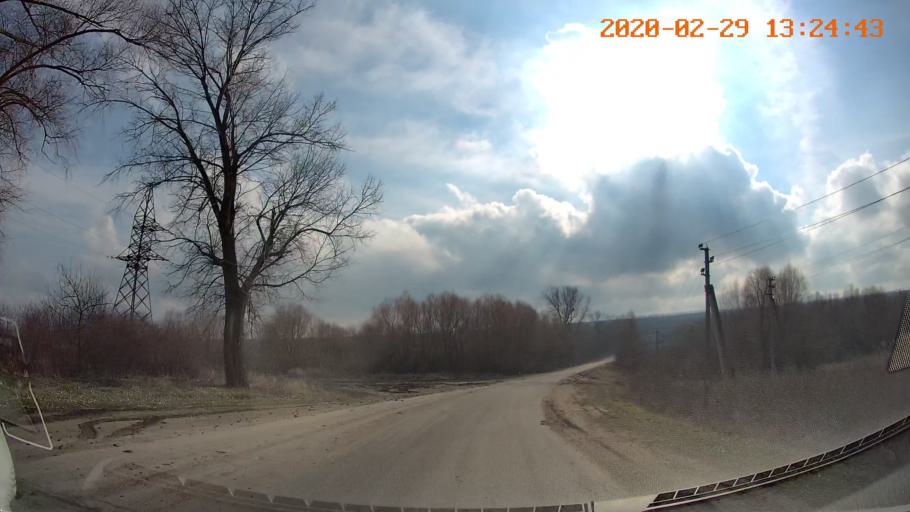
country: MD
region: Telenesti
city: Camenca
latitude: 47.9361
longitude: 28.6287
